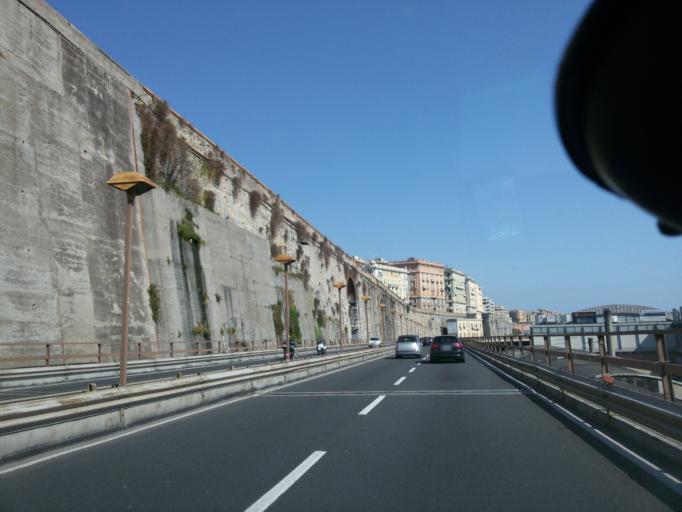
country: IT
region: Liguria
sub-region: Provincia di Genova
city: San Teodoro
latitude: 44.3978
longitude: 8.9367
